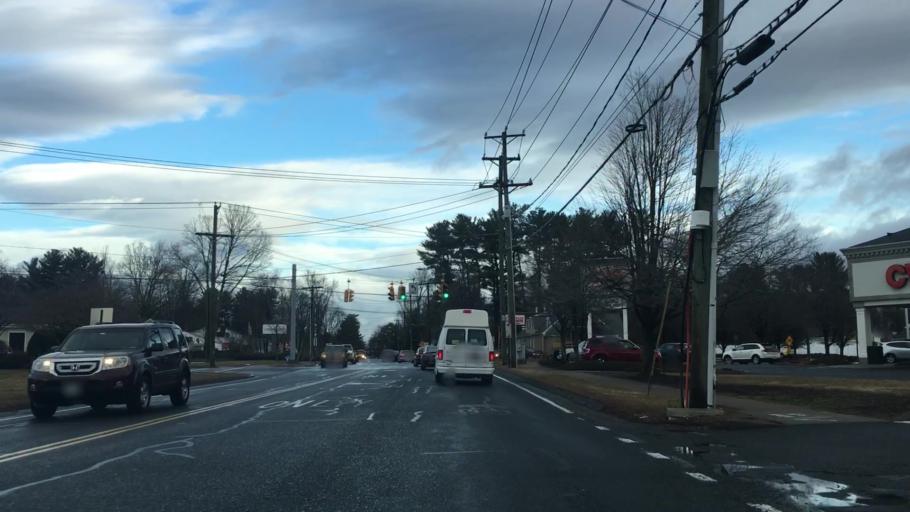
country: US
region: Massachusetts
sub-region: Hampden County
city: Agawam
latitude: 42.0614
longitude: -72.6321
